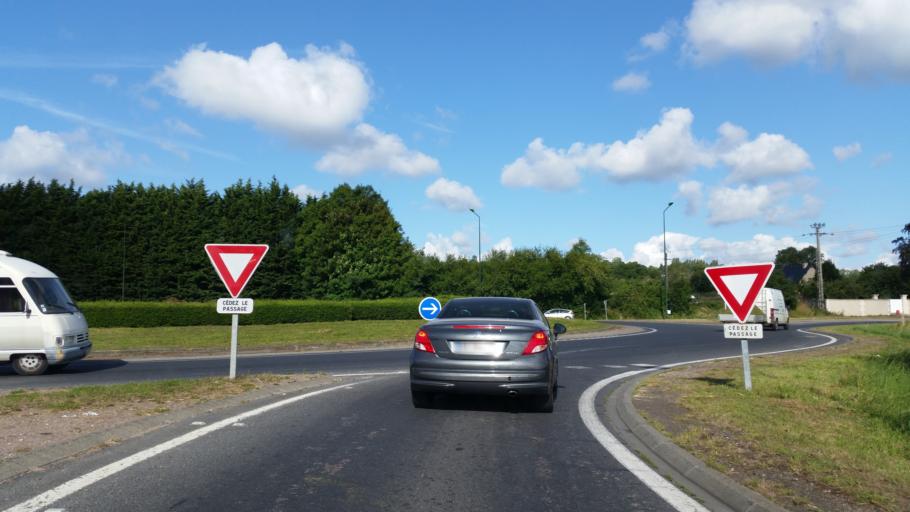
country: FR
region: Lower Normandy
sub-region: Departement du Calvados
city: Touques
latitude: 49.3332
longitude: 0.1123
